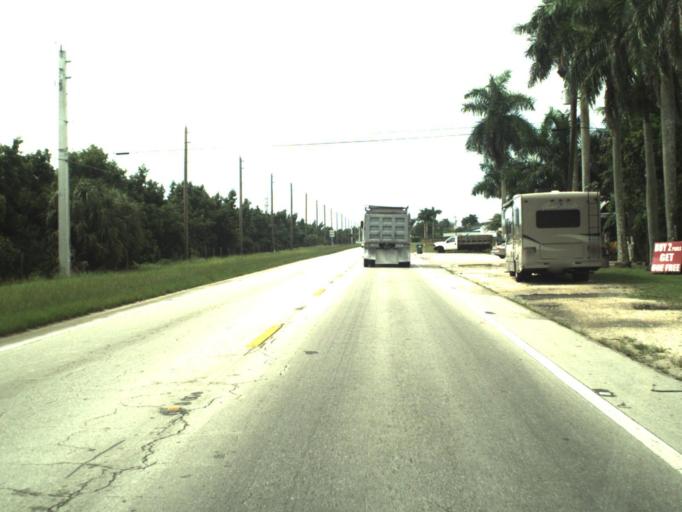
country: US
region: Florida
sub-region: Miami-Dade County
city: Richmond West
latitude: 25.5624
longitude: -80.4782
